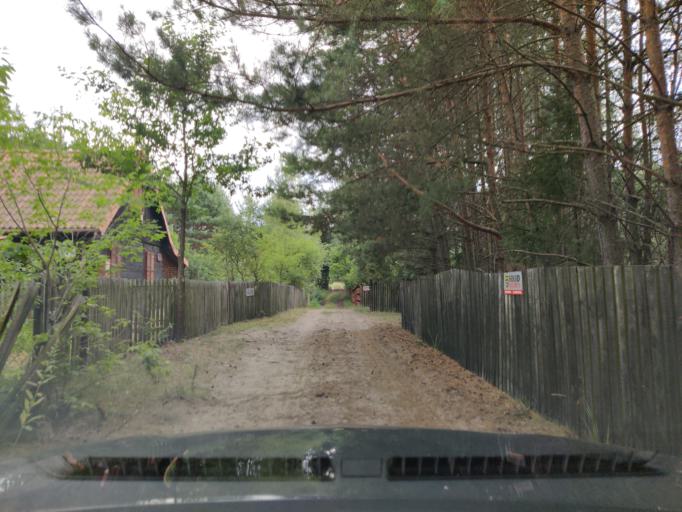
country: PL
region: Masovian Voivodeship
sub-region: Powiat pultuski
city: Pultusk
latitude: 52.7636
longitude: 21.1388
